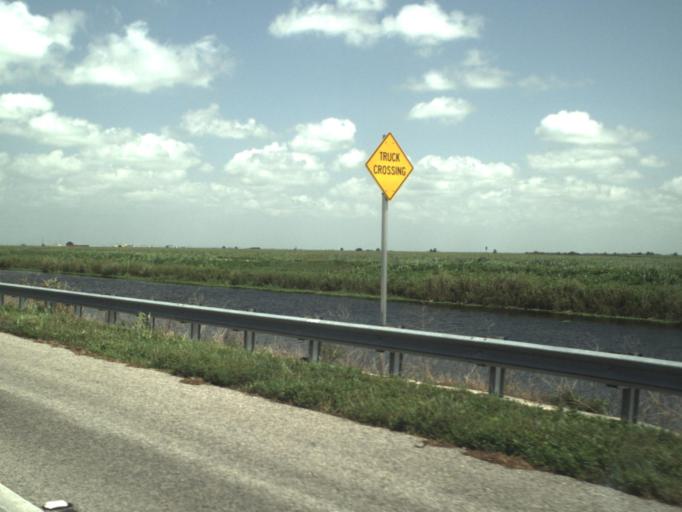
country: US
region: Florida
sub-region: Palm Beach County
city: Belle Glade Camp
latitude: 26.5495
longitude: -80.7041
